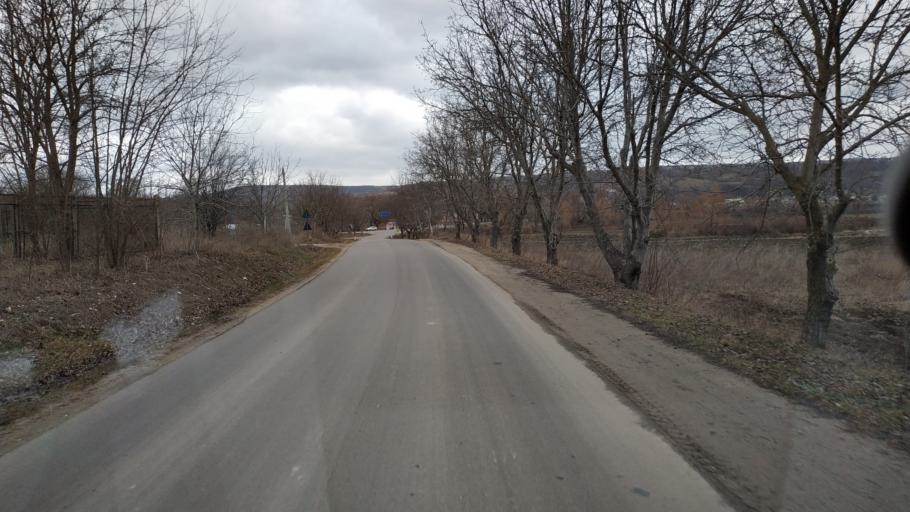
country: MD
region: Calarasi
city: Calarasi
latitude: 47.2466
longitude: 28.2865
